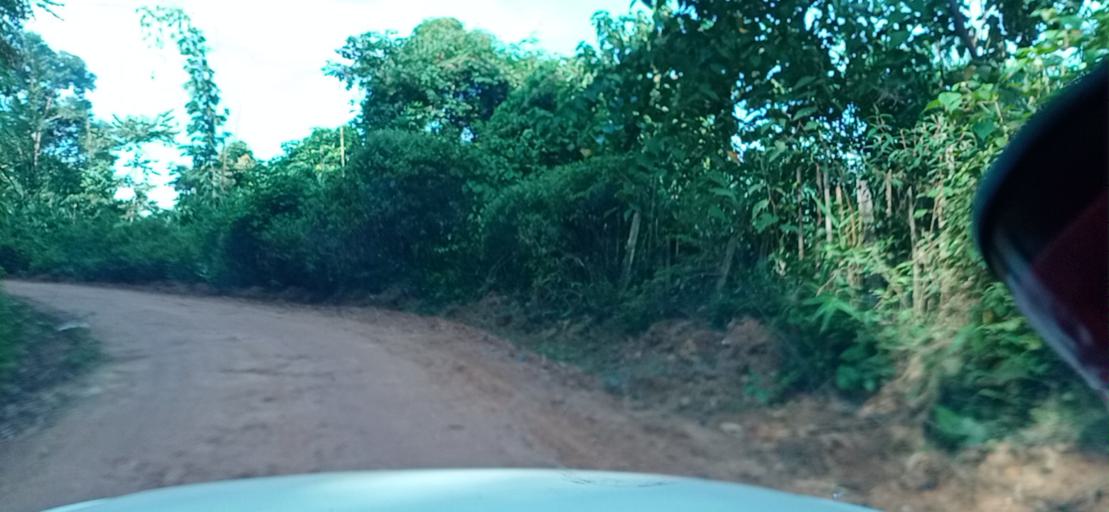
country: TH
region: Changwat Bueng Kan
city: Pak Khat
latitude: 18.6617
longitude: 103.1959
